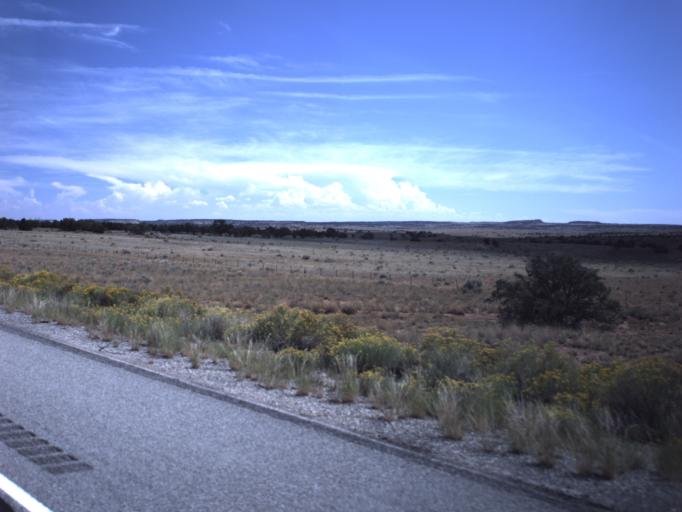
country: US
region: Utah
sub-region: Emery County
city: Castle Dale
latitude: 38.8713
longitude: -110.7297
